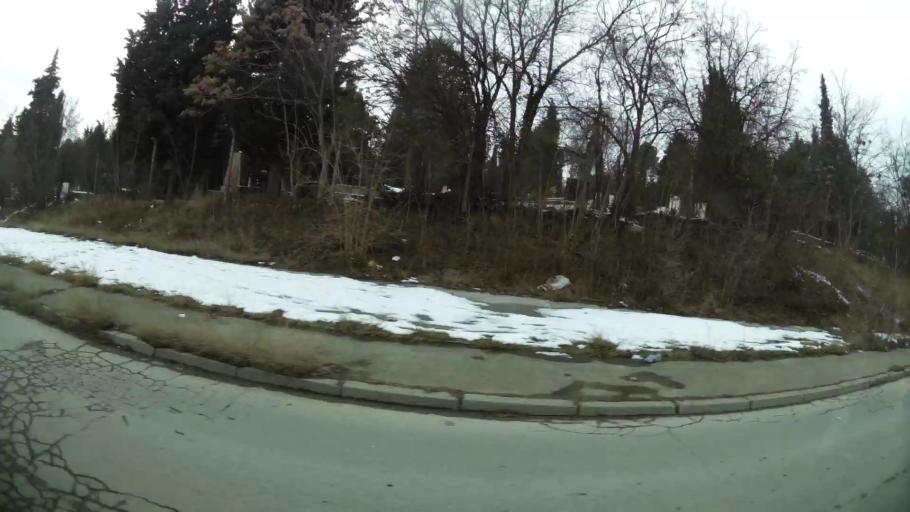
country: MK
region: Butel
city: Butel
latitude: 42.0389
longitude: 21.4376
